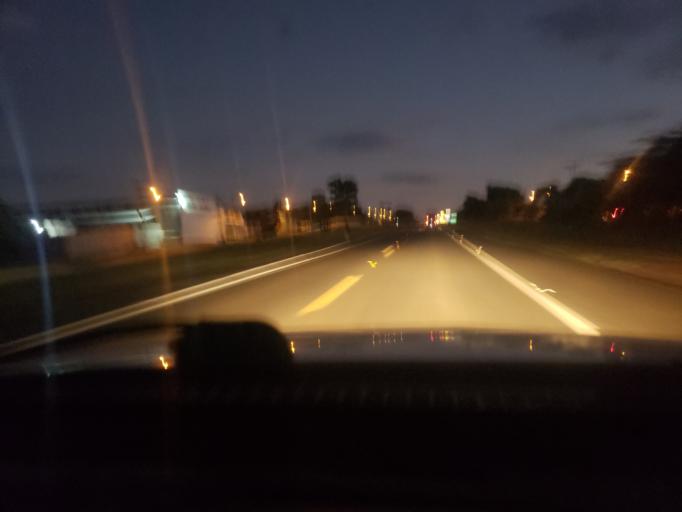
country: BR
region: Sao Paulo
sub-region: Conchal
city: Conchal
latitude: -22.3375
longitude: -47.1564
